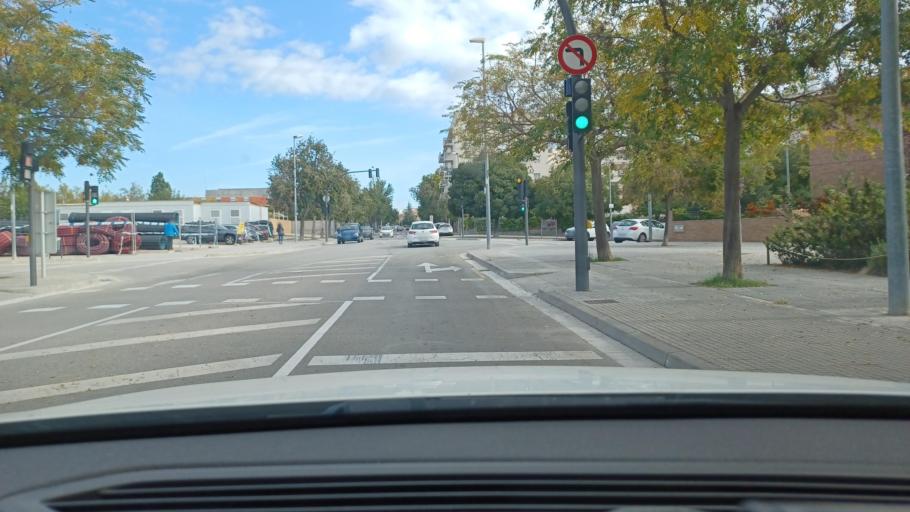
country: ES
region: Catalonia
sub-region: Provincia de Barcelona
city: Vilafranca del Penedes
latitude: 41.3383
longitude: 1.6996
